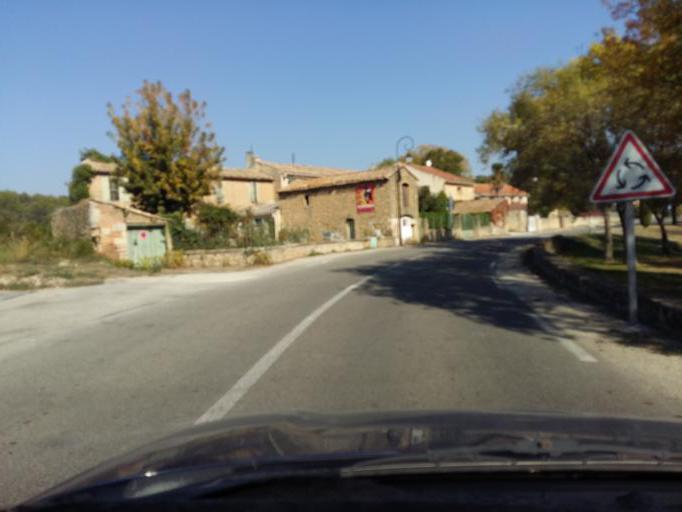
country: FR
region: Provence-Alpes-Cote d'Azur
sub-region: Departement du Vaucluse
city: Serignan-du-Comtat
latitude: 44.1918
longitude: 4.8446
